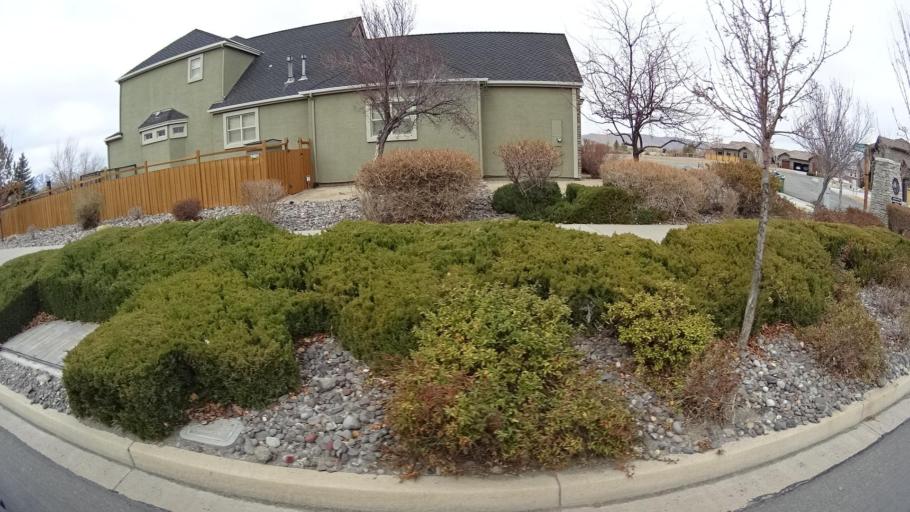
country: US
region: Nevada
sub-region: Washoe County
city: Spanish Springs
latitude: 39.6137
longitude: -119.6835
